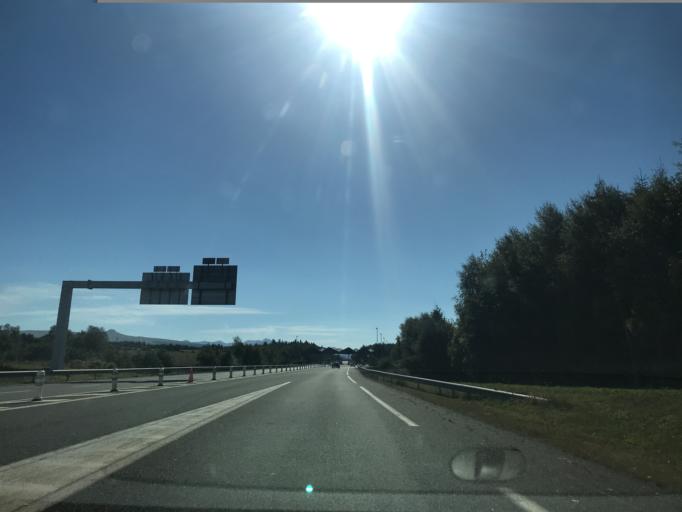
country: FR
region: Auvergne
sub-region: Departement du Puy-de-Dome
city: Saint-Sauves-d'Auvergne
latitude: 45.6696
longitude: 2.6802
